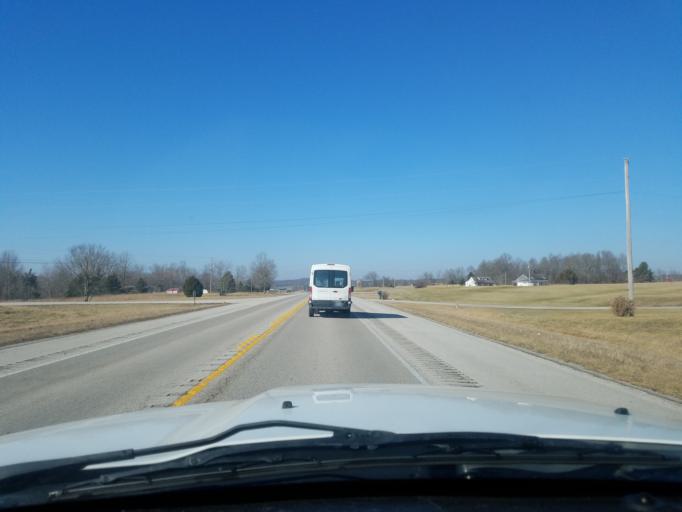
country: US
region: Kentucky
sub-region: Green County
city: Greensburg
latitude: 37.4155
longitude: -85.5001
